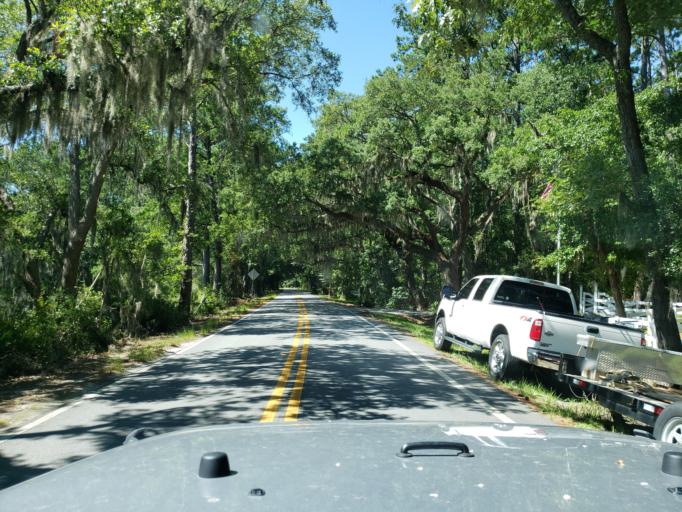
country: US
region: Georgia
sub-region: Chatham County
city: Georgetown
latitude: 31.9670
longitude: -81.2185
